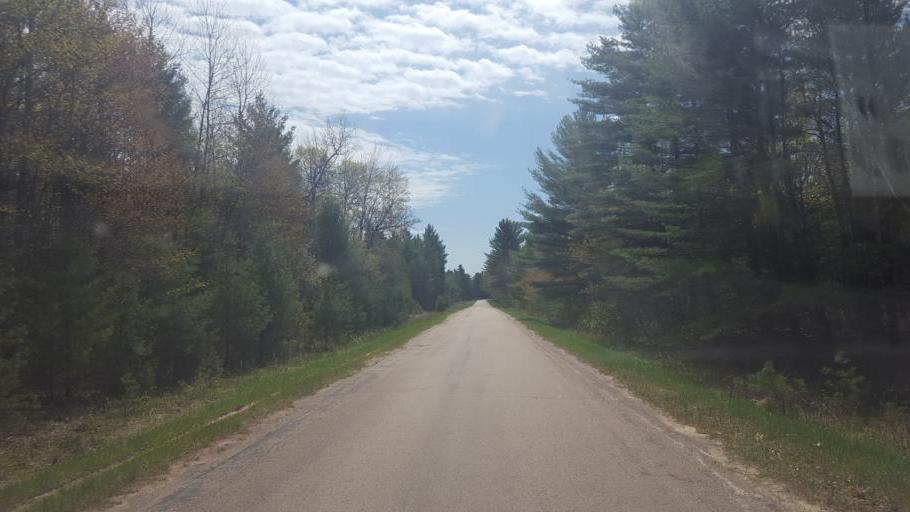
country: US
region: Wisconsin
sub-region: Clark County
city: Neillsville
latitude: 44.3097
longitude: -90.5053
